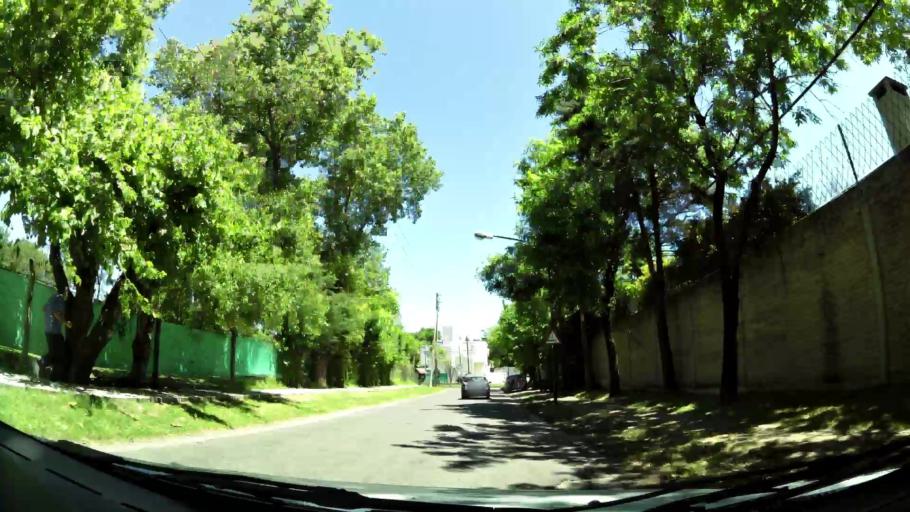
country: AR
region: Buenos Aires
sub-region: Partido de San Isidro
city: San Isidro
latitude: -34.4963
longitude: -58.5721
